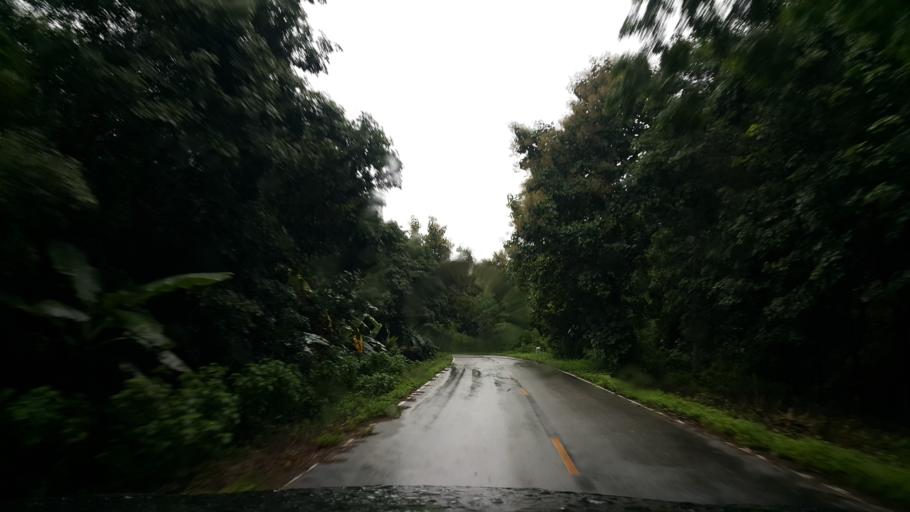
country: TH
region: Phayao
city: Phu Sang
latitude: 19.6109
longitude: 100.4079
